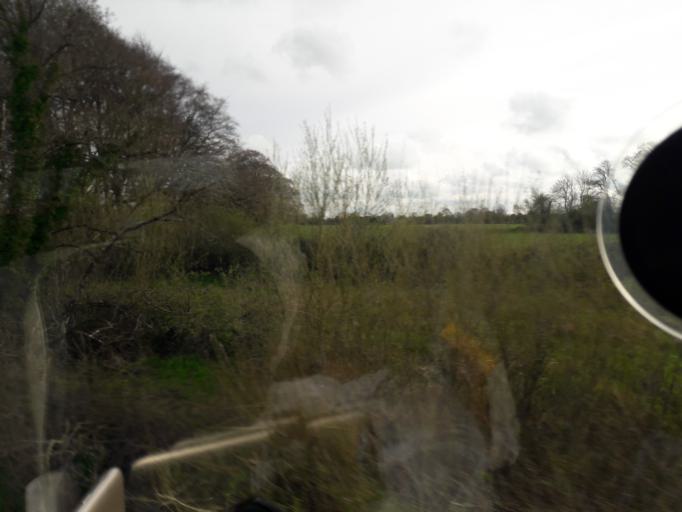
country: IE
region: Leinster
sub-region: An Mhi
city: Longwood
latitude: 53.4413
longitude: -6.9300
